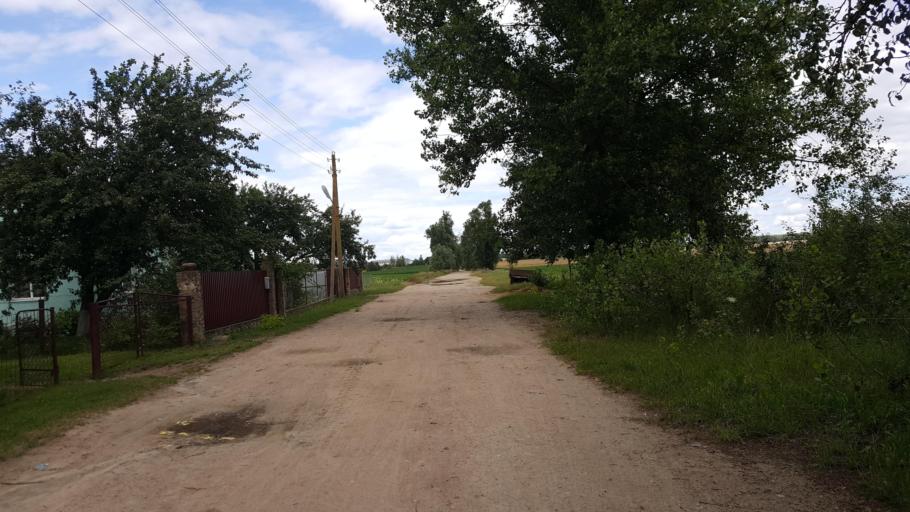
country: BY
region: Brest
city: Kamyanyets
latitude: 52.3625
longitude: 23.9102
